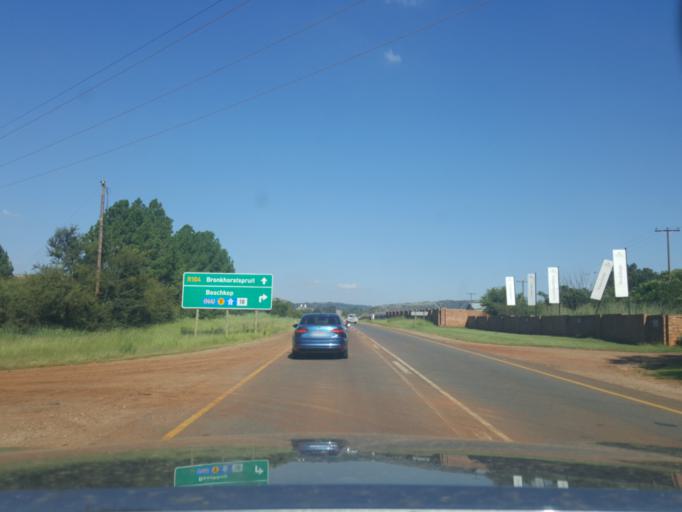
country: ZA
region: Gauteng
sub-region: City of Tshwane Metropolitan Municipality
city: Cullinan
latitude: -25.7664
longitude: 28.4306
